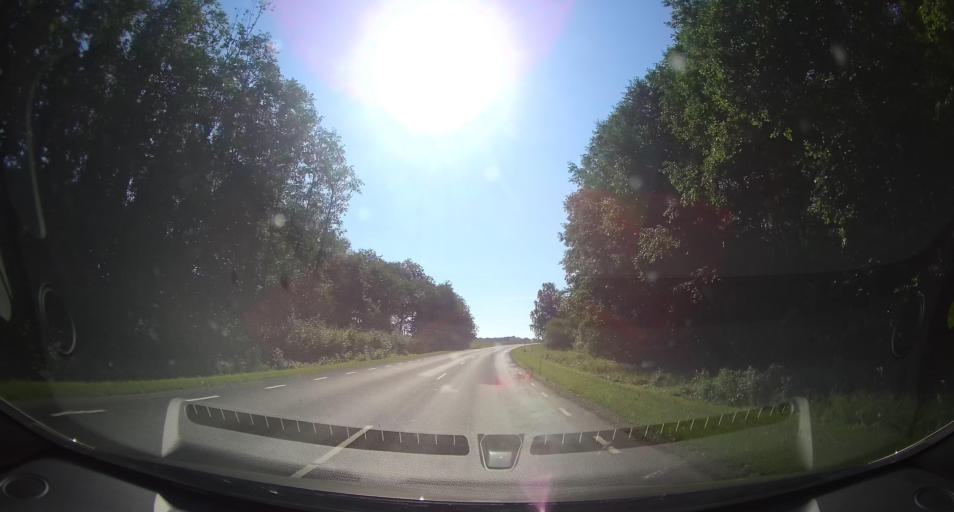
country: EE
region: Harju
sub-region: Raasiku vald
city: Arukula
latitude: 59.3431
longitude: 25.1278
